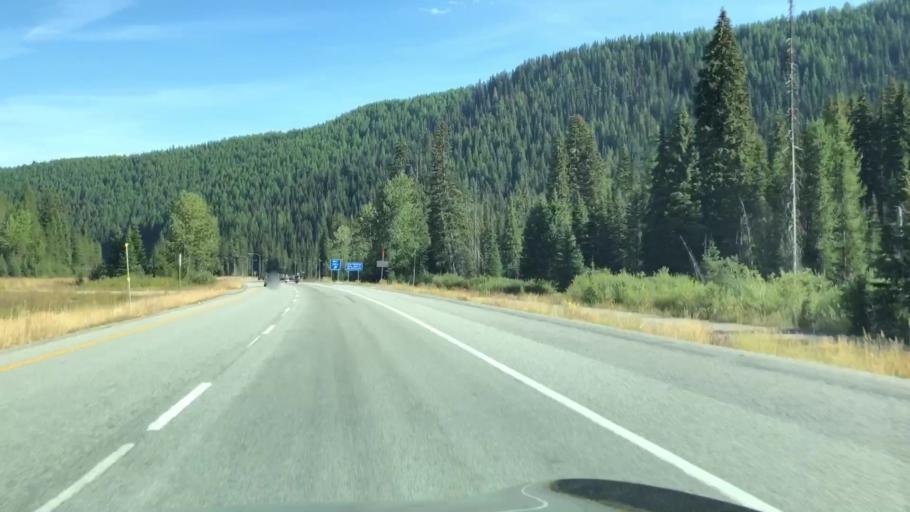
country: US
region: Idaho
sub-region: Shoshone County
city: Wallace
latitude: 47.4226
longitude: -115.6346
